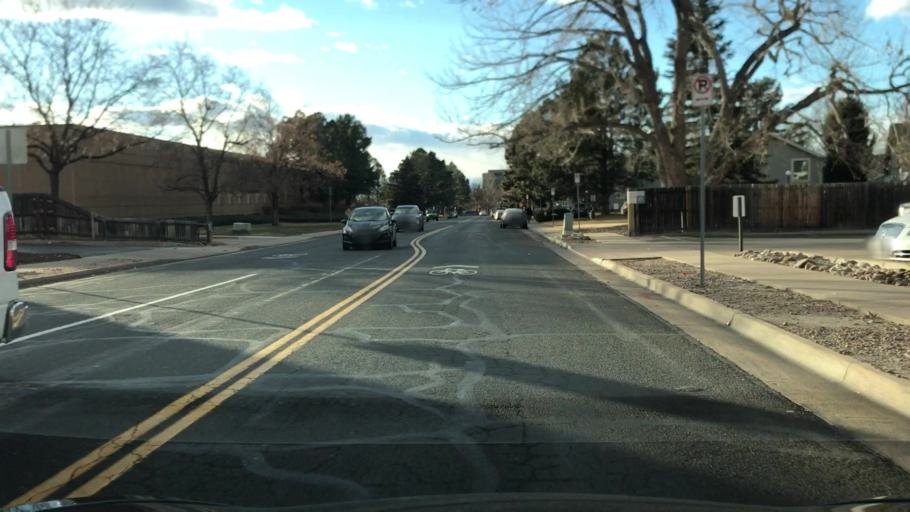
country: US
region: Colorado
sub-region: Adams County
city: Aurora
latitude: 39.6617
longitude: -104.8480
